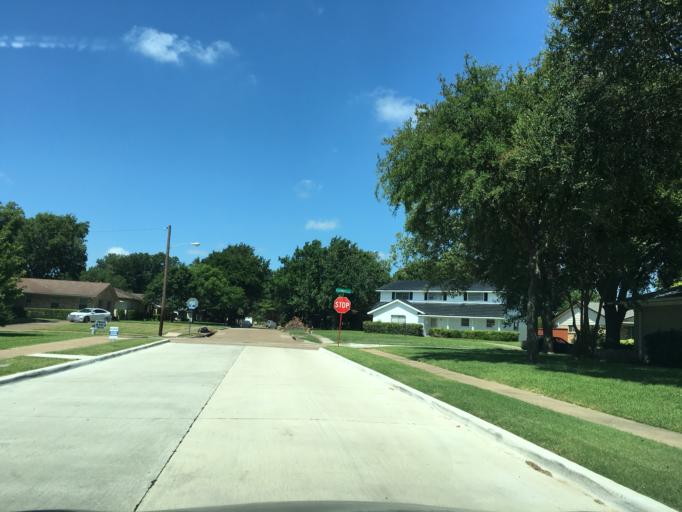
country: US
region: Texas
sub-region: Dallas County
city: Garland
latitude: 32.8478
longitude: -96.6519
